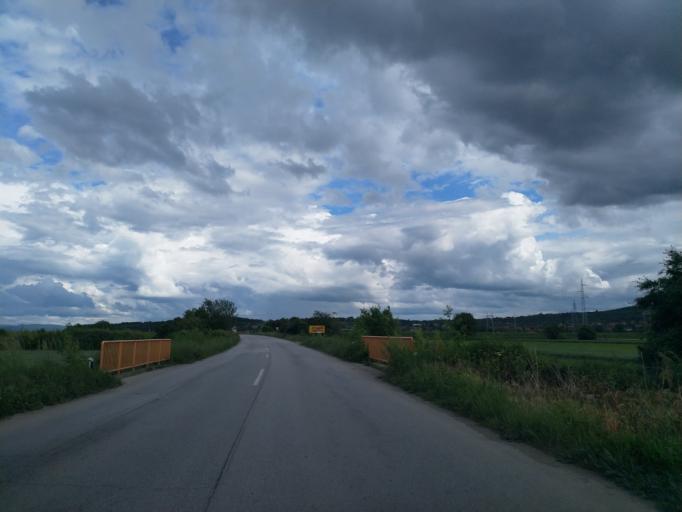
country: RS
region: Central Serbia
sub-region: Pomoravski Okrug
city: Jagodina
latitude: 43.9593
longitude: 21.2861
